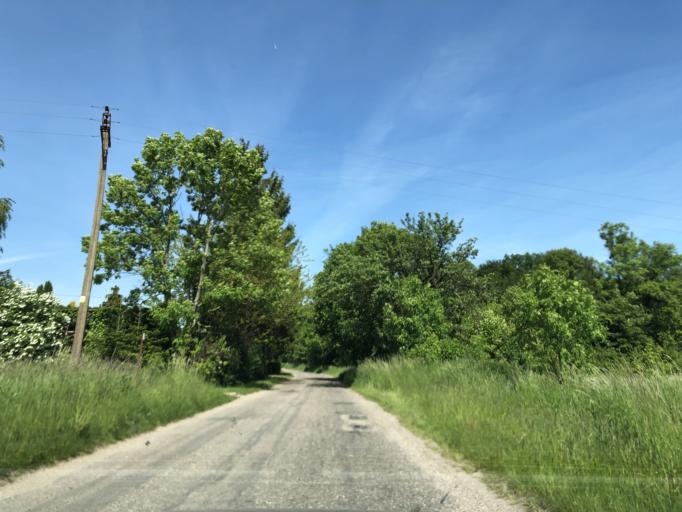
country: PL
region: West Pomeranian Voivodeship
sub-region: Powiat kolobrzeski
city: Goscino
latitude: 54.0071
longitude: 15.7234
